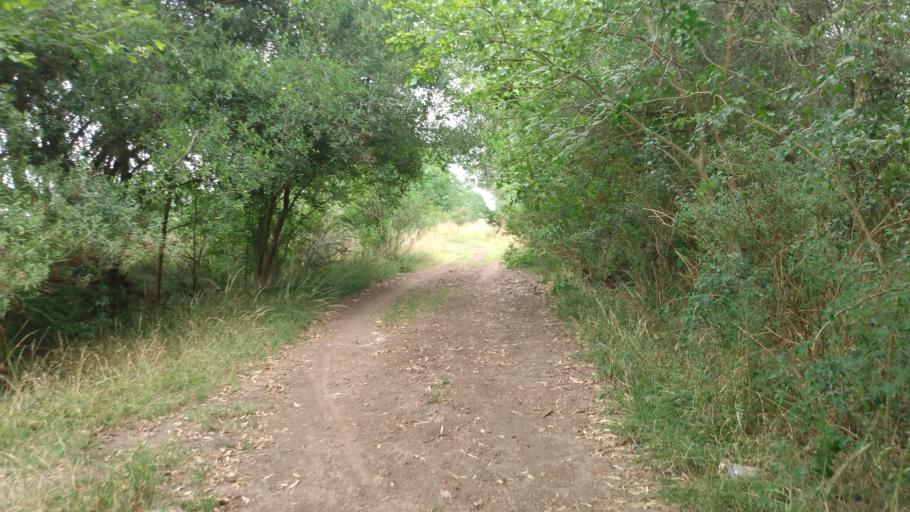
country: AR
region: Buenos Aires
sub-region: Partido de Lujan
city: Lujan
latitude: -34.6022
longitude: -59.0668
